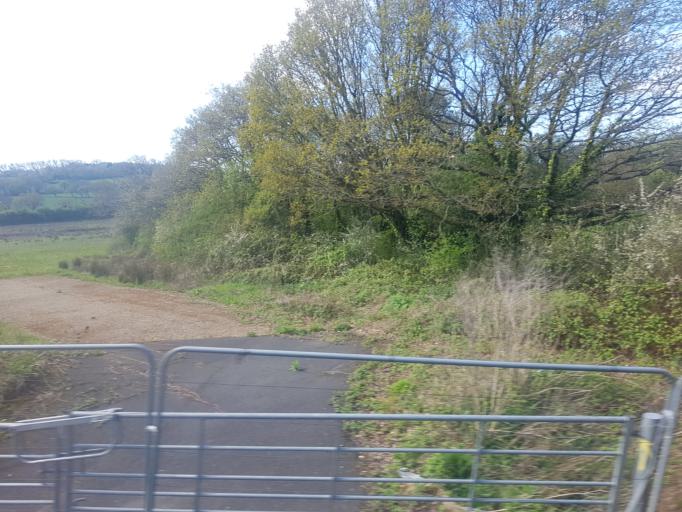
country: GB
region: England
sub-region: Isle of Wight
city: Newport
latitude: 50.7251
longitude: -1.2606
